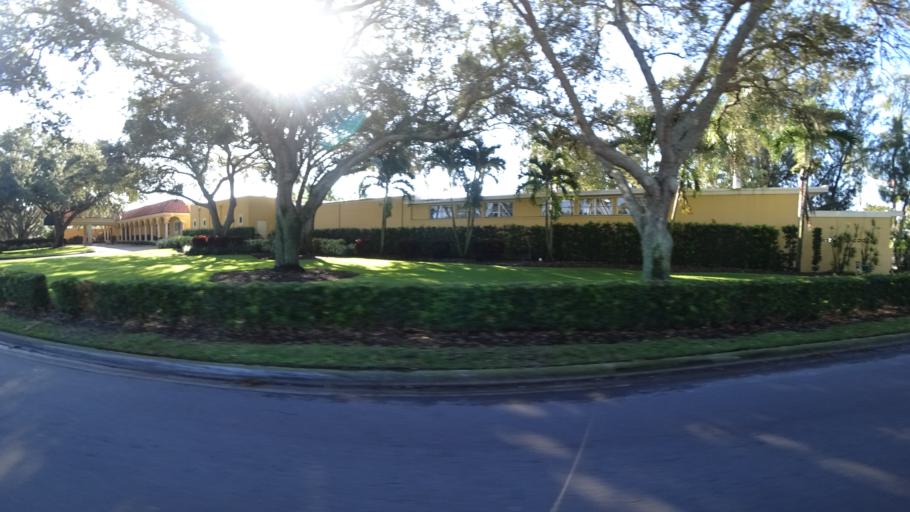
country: US
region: Florida
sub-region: Manatee County
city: West Bradenton
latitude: 27.4925
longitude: -82.6092
